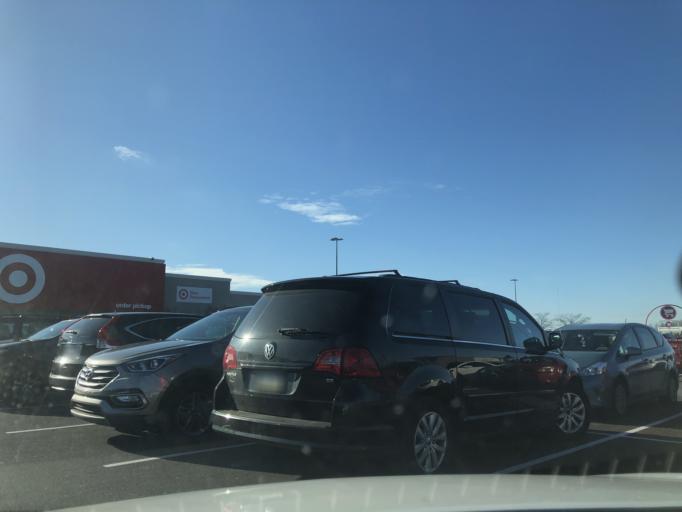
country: US
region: Pennsylvania
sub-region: Bucks County
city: Trevose
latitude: 40.1359
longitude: -74.9610
